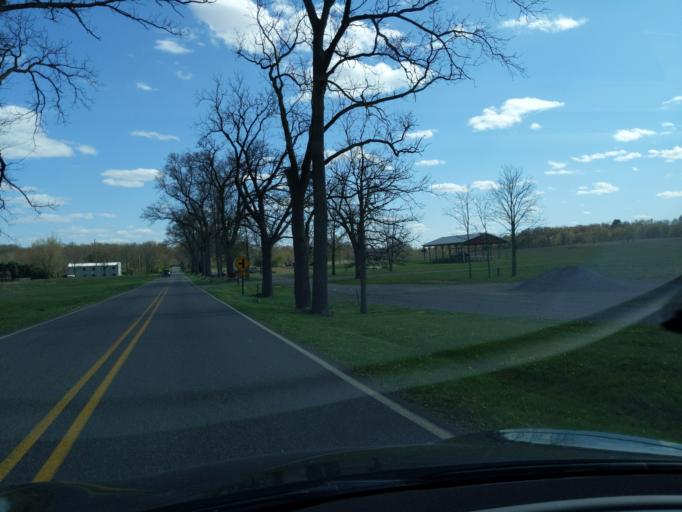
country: US
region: Michigan
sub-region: Ingham County
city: Leslie
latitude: 42.3811
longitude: -84.5416
